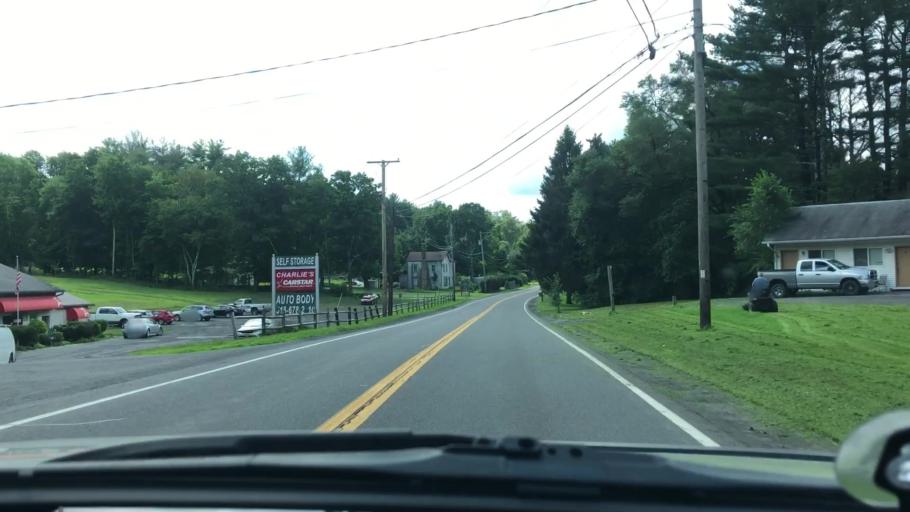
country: US
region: New York
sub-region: Greene County
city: Palenville
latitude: 42.1842
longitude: -73.9854
